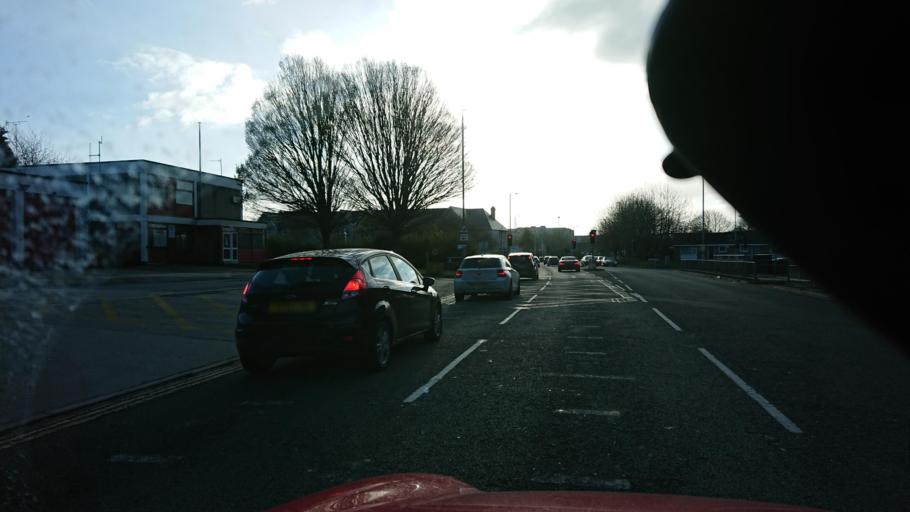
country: GB
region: England
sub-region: Cornwall
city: Torpoint
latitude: 50.3975
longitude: -4.1769
